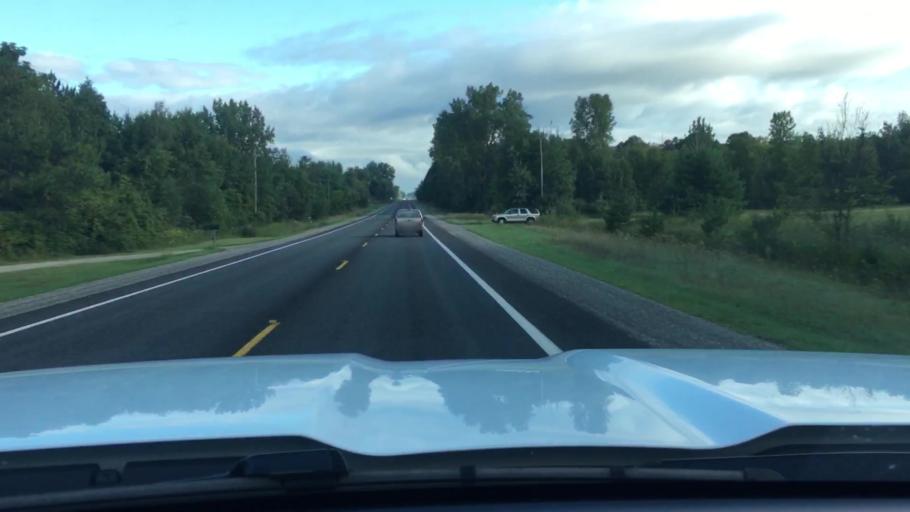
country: US
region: Michigan
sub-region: Tuscola County
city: Caro
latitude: 43.3591
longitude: -83.3828
